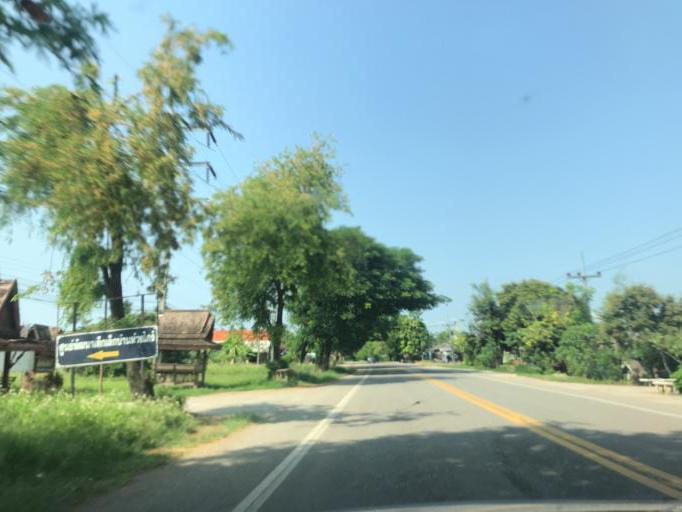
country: TH
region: Phayao
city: Chun
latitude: 19.4264
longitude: 100.1805
